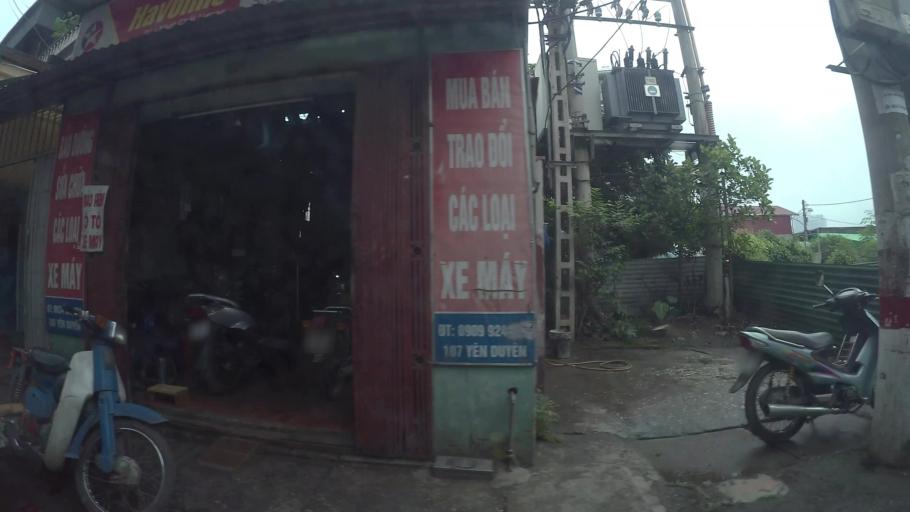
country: VN
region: Ha Noi
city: Van Dien
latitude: 20.9712
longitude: 105.8695
